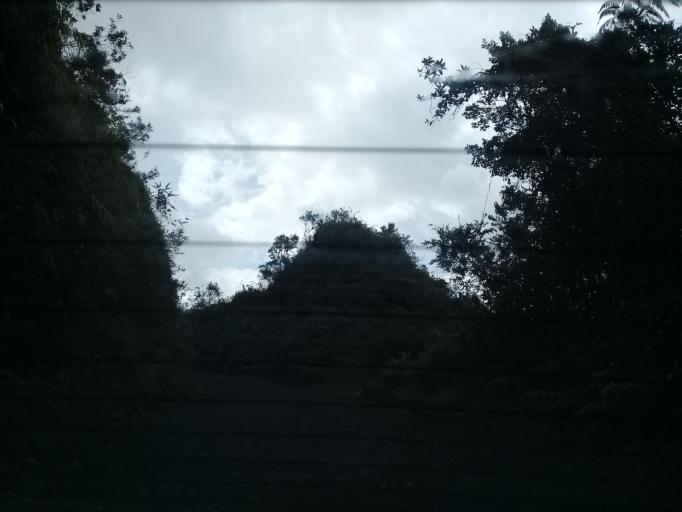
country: CO
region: Cundinamarca
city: Gachala
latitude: 4.7031
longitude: -73.4290
